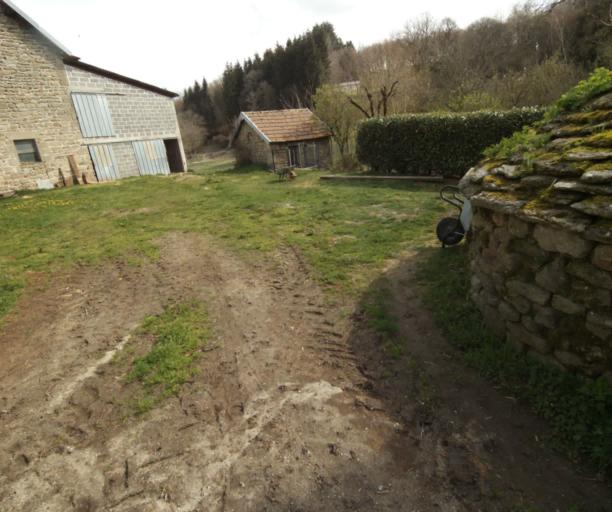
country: FR
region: Limousin
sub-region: Departement de la Correze
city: Correze
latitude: 45.3859
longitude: 1.8976
